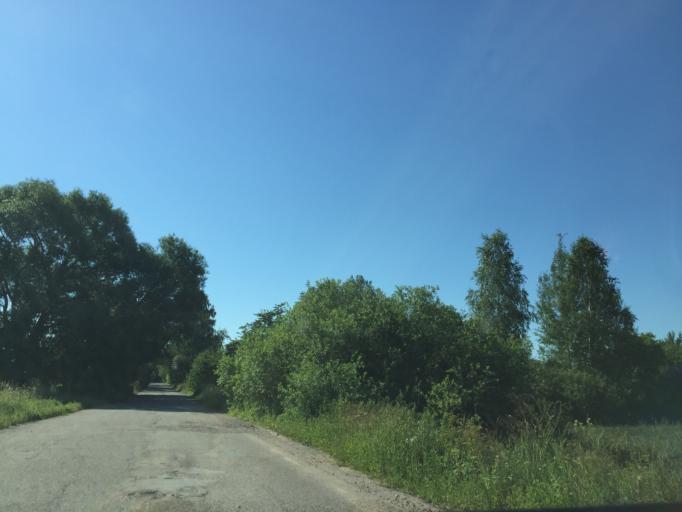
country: LV
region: Vilanu
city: Vilani
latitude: 56.5752
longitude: 26.9171
